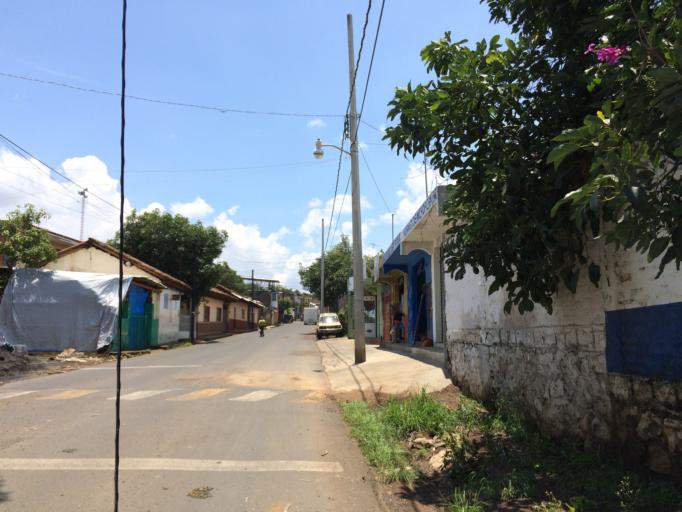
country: MX
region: Michoacan
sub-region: Periban
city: San Francisco Periban
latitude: 19.5562
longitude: -102.3996
